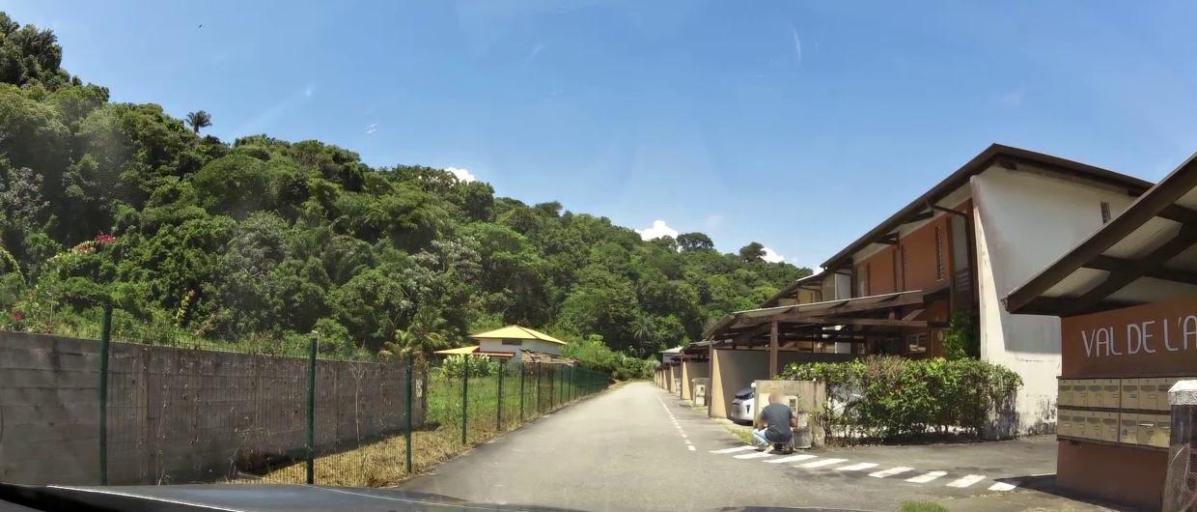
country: GF
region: Guyane
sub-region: Guyane
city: Remire-Montjoly
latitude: 4.9232
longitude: -52.2859
